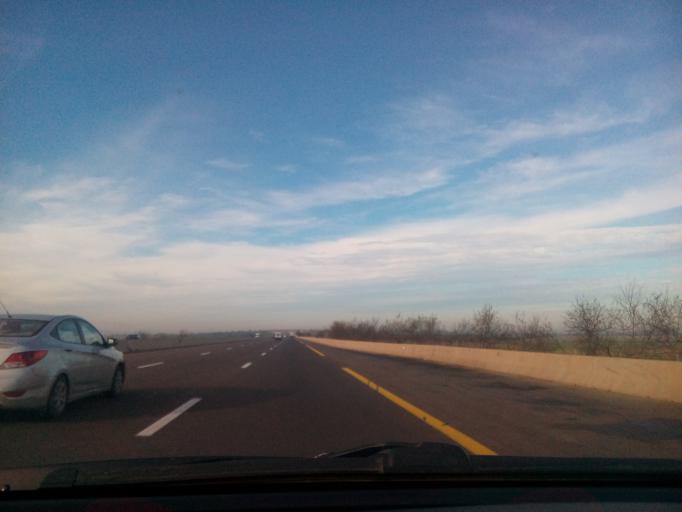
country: DZ
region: Mascara
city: Sig
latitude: 35.6168
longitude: 0.0160
